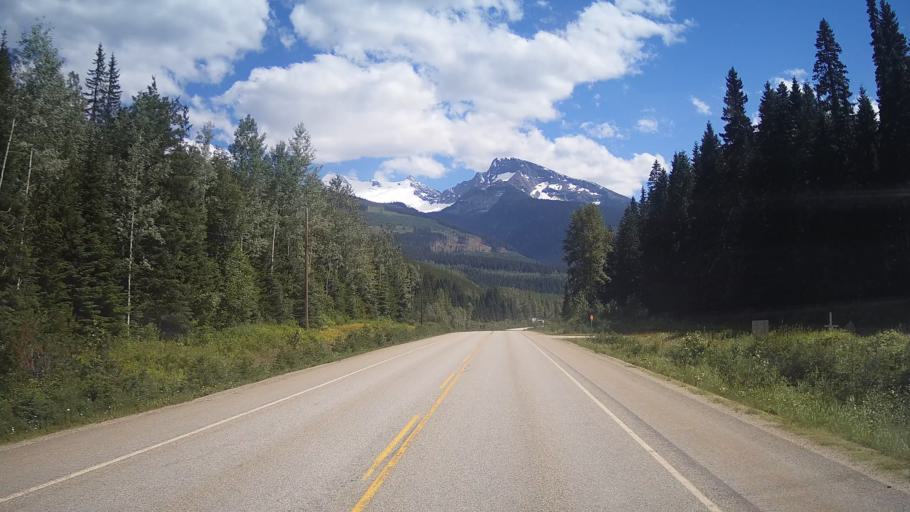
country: CA
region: Alberta
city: Jasper Park Lodge
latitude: 52.5900
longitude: -119.0984
